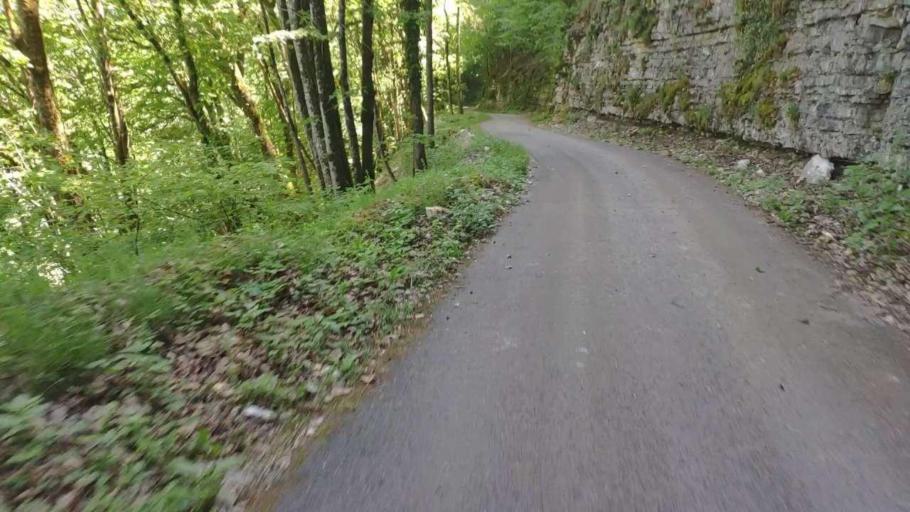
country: FR
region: Franche-Comte
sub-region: Departement du Jura
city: Poligny
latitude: 46.7458
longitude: 5.6765
